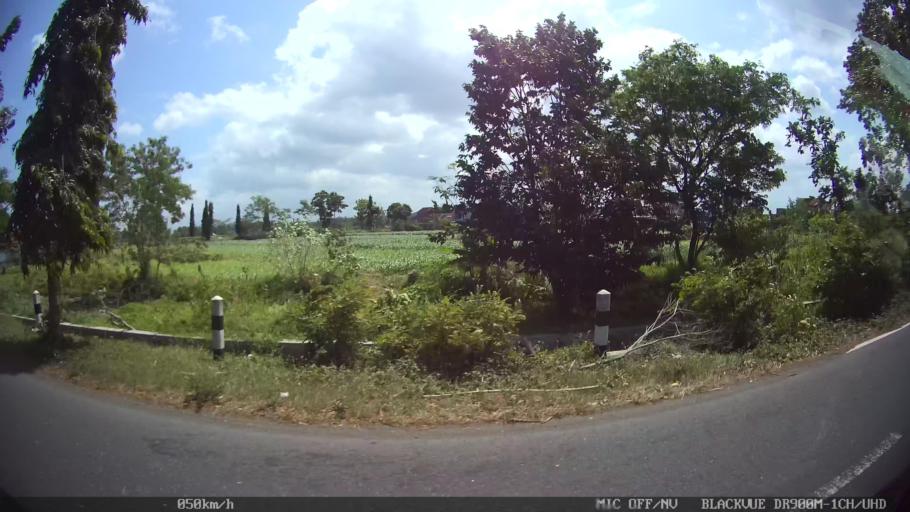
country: ID
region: Daerah Istimewa Yogyakarta
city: Pandak
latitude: -7.9093
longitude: 110.2982
